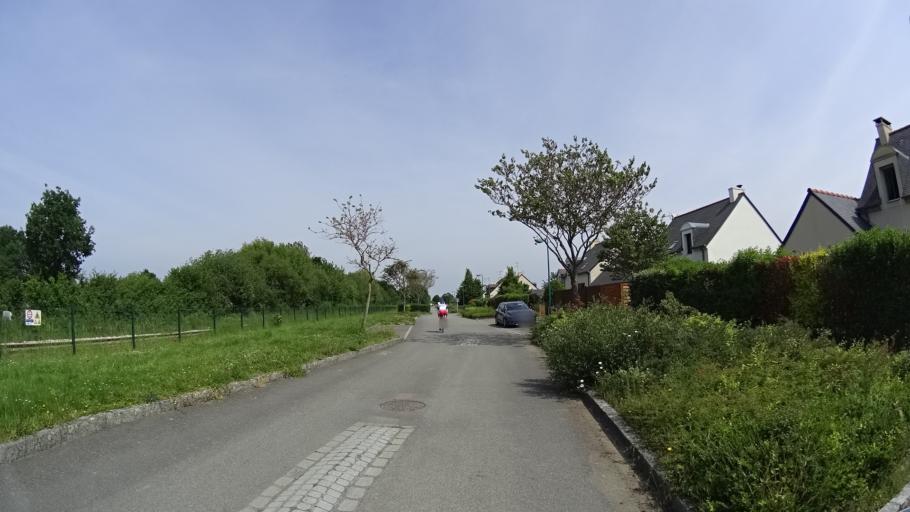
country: FR
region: Brittany
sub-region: Departement d'Ille-et-Vilaine
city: Saint-Armel
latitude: 48.0159
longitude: -1.5947
